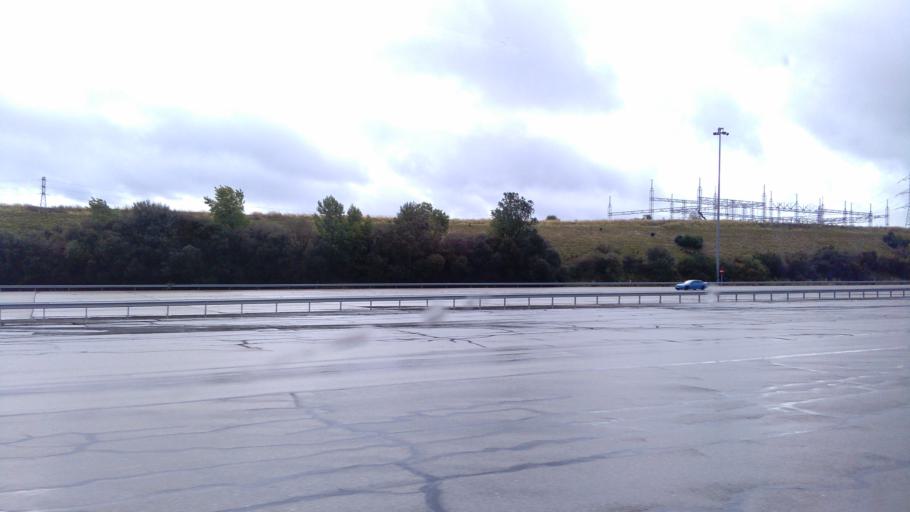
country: ES
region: Madrid
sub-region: Provincia de Madrid
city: Leganes
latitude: 40.3500
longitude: -3.7824
